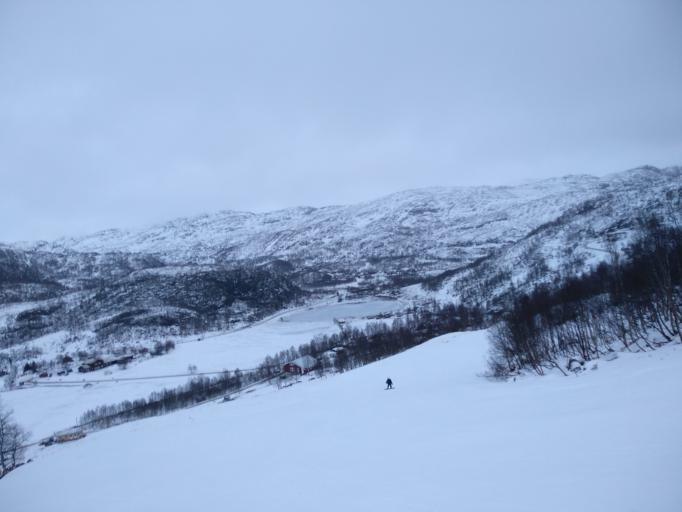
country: NO
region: Vest-Agder
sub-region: Sirdal
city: Tonstad
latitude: 59.0222
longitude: 6.9178
